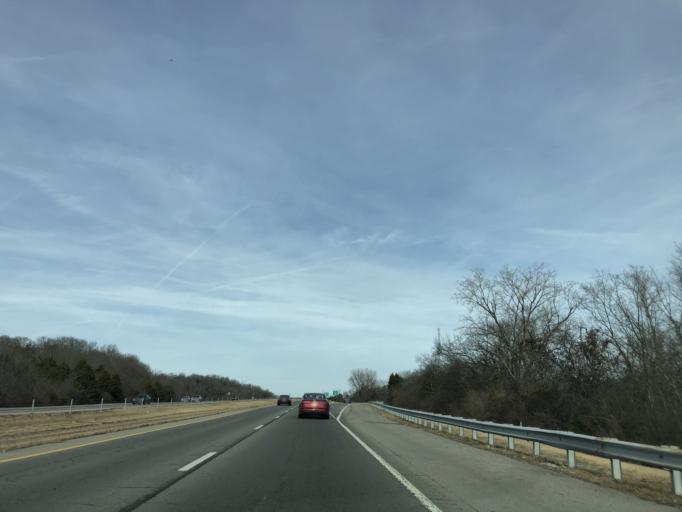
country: US
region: Tennessee
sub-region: Davidson County
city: Nashville
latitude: 36.2140
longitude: -86.7482
